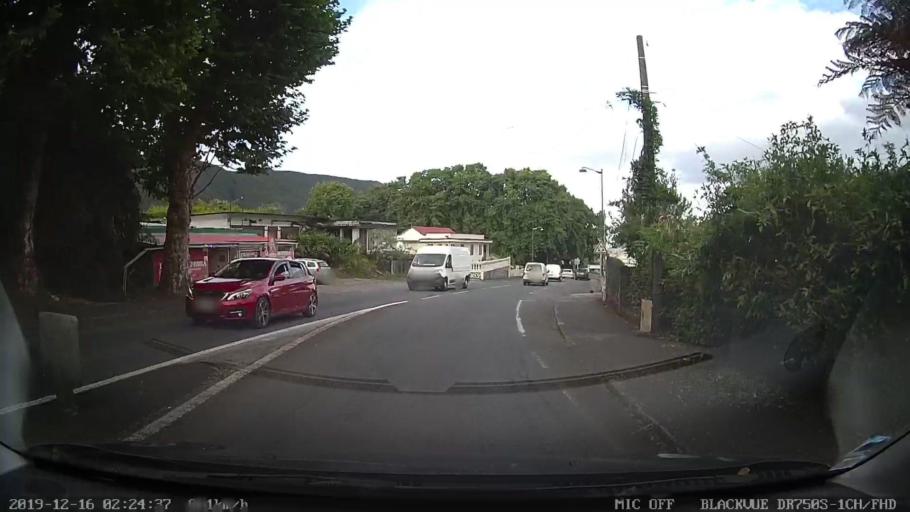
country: RE
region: Reunion
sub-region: Reunion
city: Saint-Benoit
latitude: -21.1365
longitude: 55.6246
